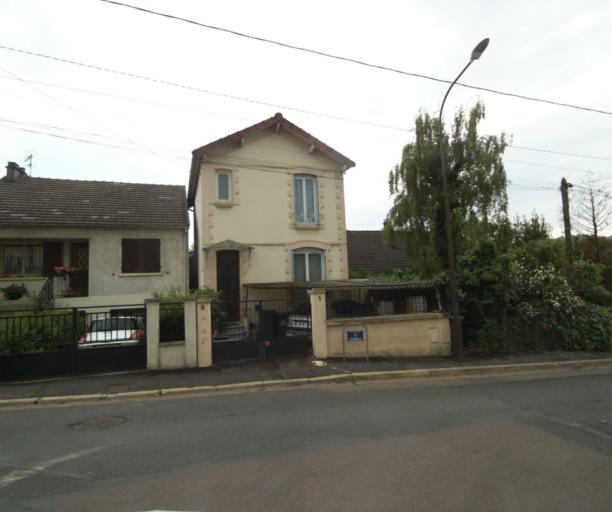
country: FR
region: Ile-de-France
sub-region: Departement du Val-d'Oise
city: Bezons
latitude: 48.9443
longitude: 2.2261
